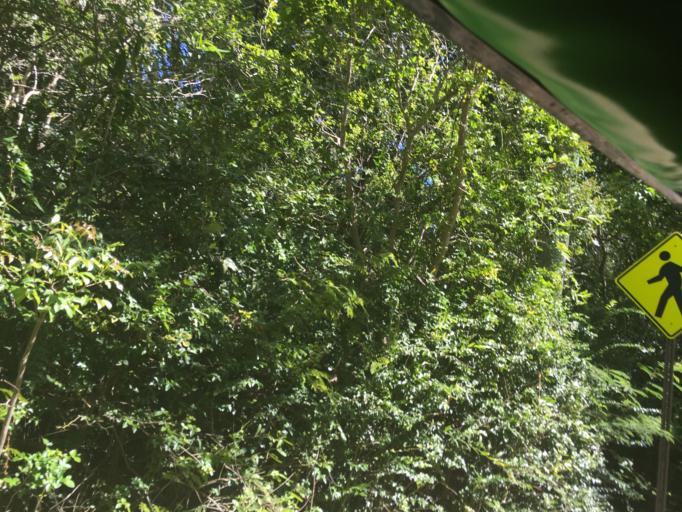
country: VI
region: Saint John Island
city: Cruz Bay
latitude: 18.3510
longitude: -64.7749
